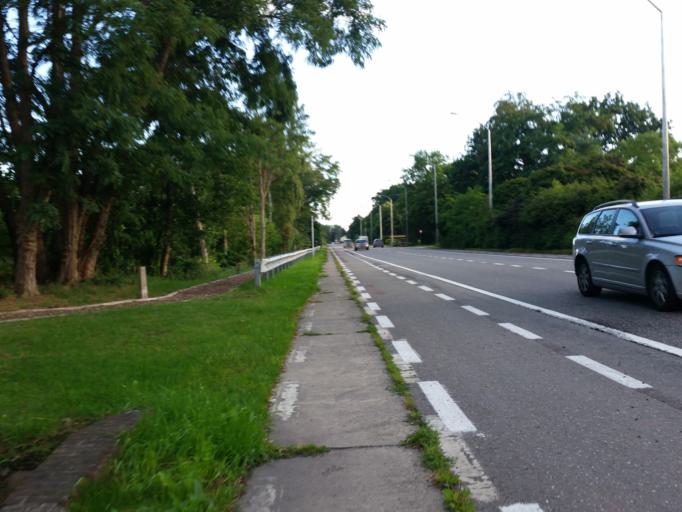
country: BE
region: Flanders
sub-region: Provincie Antwerpen
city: Duffel
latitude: 51.0757
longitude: 4.4903
